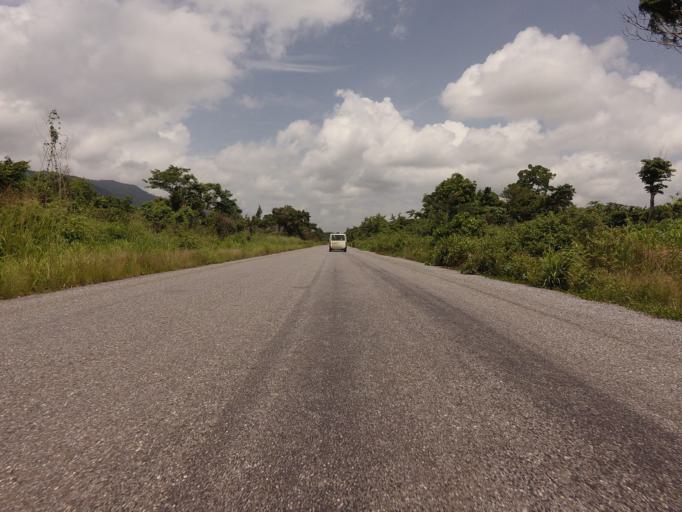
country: GH
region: Volta
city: Kpandu
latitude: 6.8362
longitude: 0.3830
